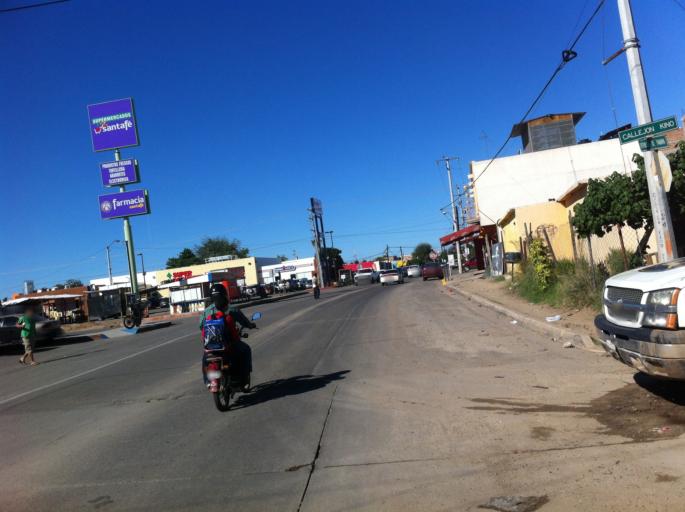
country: MX
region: Sonora
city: Hermosillo
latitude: 29.1027
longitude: -111.0054
